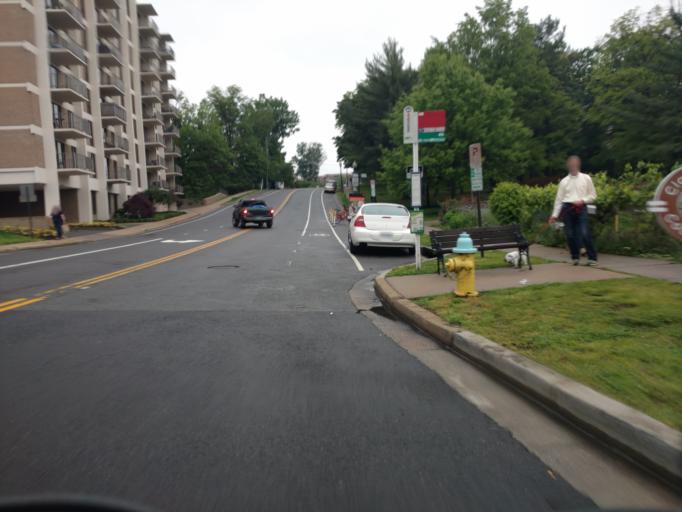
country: US
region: Virginia
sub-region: Arlington County
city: Arlington
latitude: 38.8830
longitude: -77.0875
